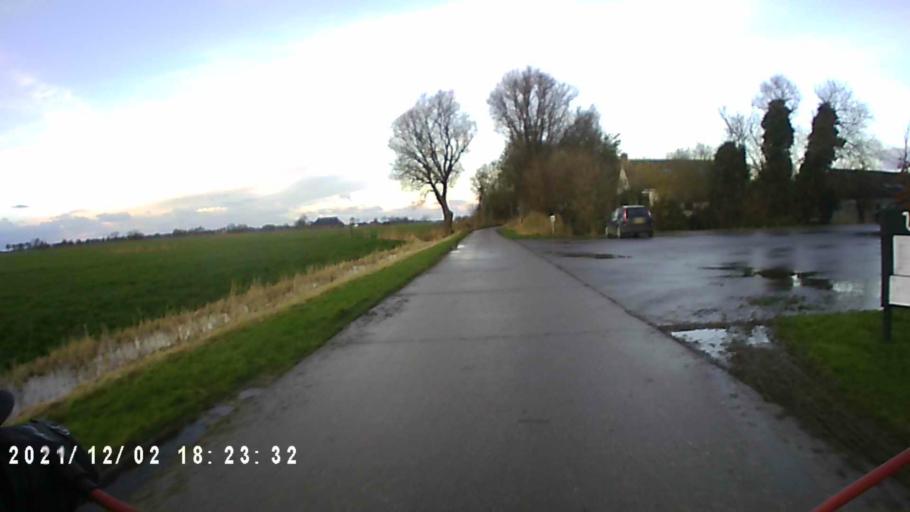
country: NL
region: Groningen
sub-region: Gemeente Groningen
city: Korrewegwijk
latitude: 53.2763
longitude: 6.5462
